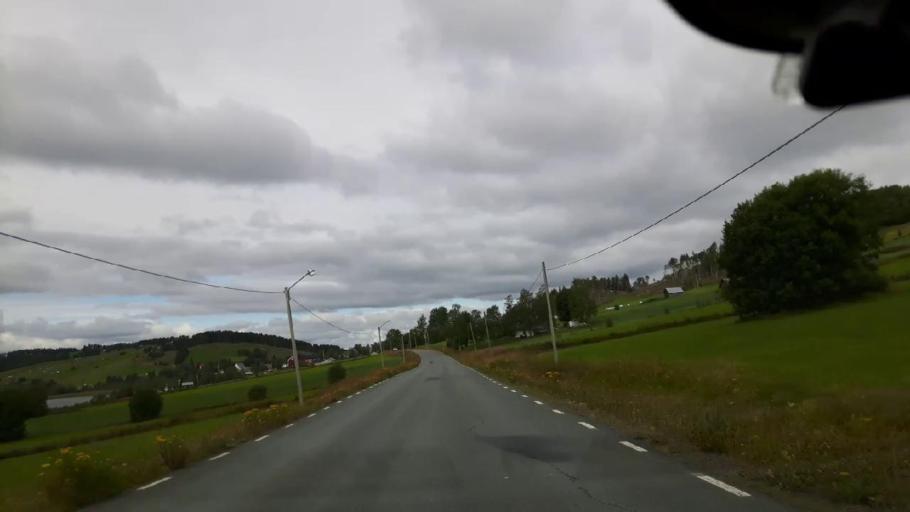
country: SE
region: Jaemtland
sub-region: Krokoms Kommun
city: Valla
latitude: 63.4884
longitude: 13.9158
